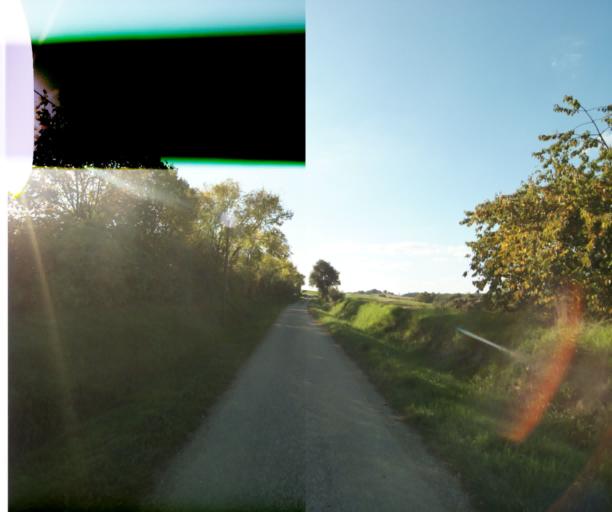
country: FR
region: Midi-Pyrenees
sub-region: Departement du Gers
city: Eauze
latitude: 43.7633
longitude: 0.1530
